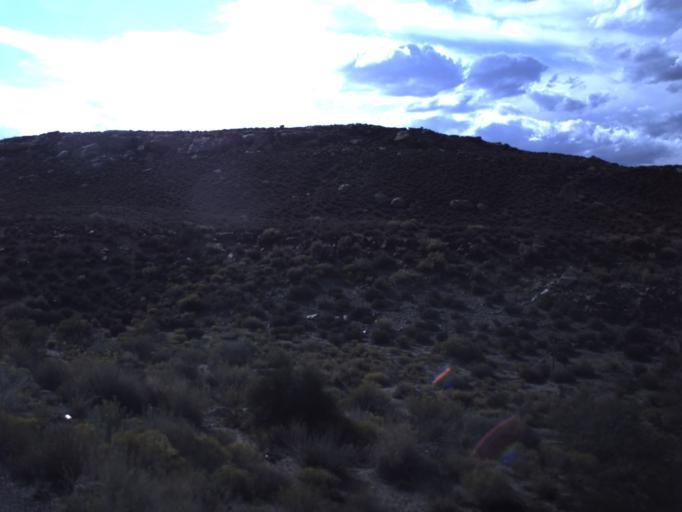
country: US
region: Utah
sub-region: San Juan County
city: Blanding
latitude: 37.3273
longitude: -109.3261
